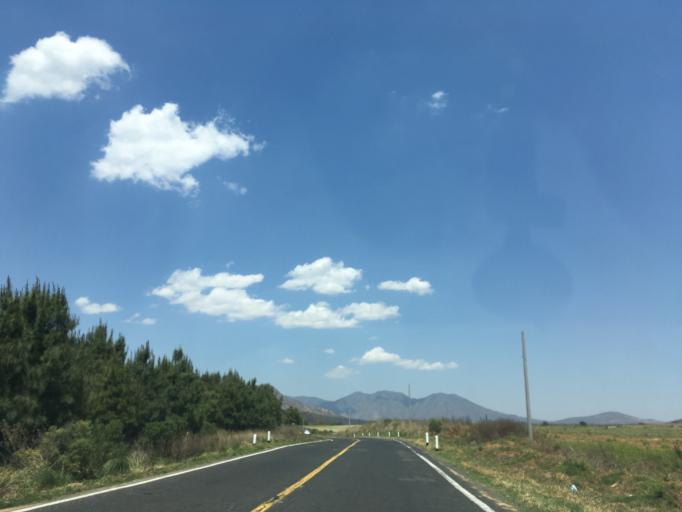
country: MX
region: Mexico
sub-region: Chalco
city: Zopoco
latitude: 19.7894
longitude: -102.0236
